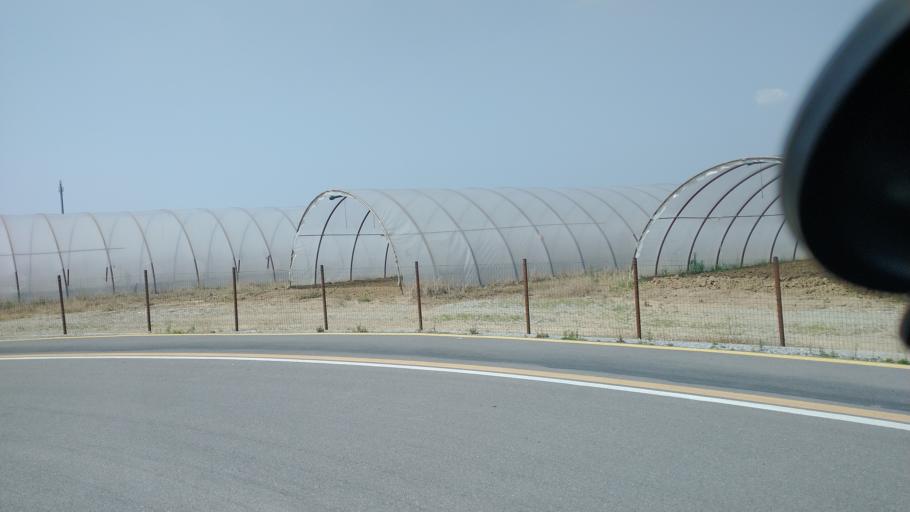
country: IT
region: Lombardy
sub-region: Provincia di Bergamo
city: Levate
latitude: 45.6224
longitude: 9.6309
